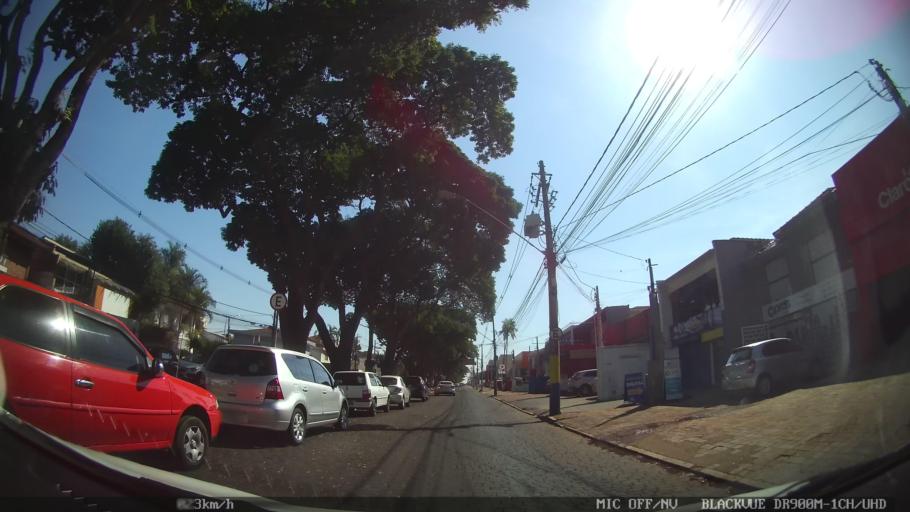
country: BR
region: Sao Paulo
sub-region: Ribeirao Preto
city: Ribeirao Preto
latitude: -21.1844
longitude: -47.8122
